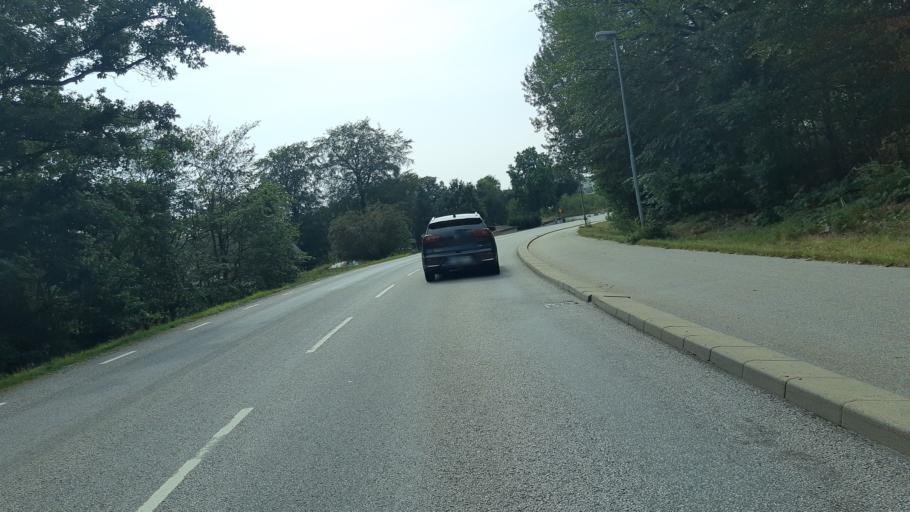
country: SE
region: Blekinge
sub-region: Ronneby Kommun
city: Ronneby
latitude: 56.1784
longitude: 15.3038
